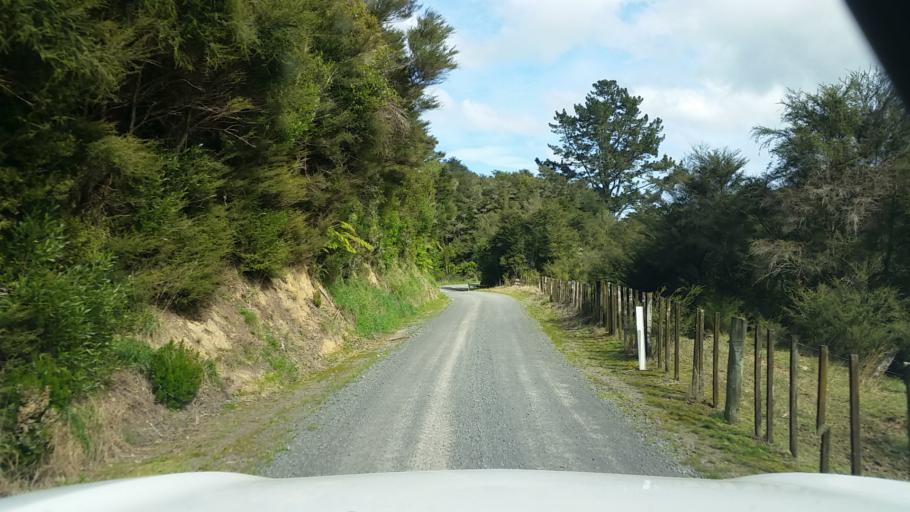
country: NZ
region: Waikato
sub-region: Hauraki District
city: Ngatea
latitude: -37.4771
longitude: 175.4556
